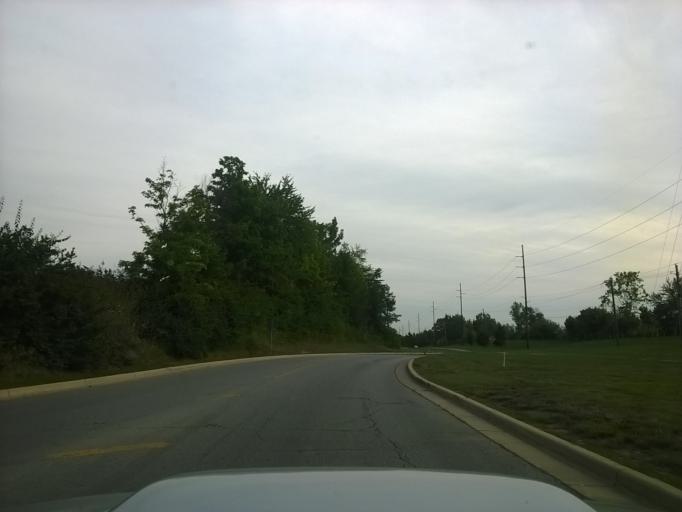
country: US
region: Indiana
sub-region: Hamilton County
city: Carmel
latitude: 39.9411
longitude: -86.0885
